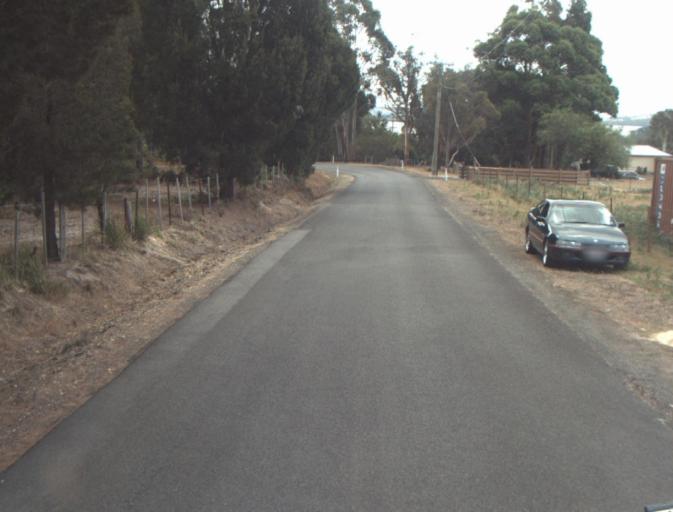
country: AU
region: Tasmania
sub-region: Launceston
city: Mayfield
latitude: -41.2830
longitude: 147.0215
